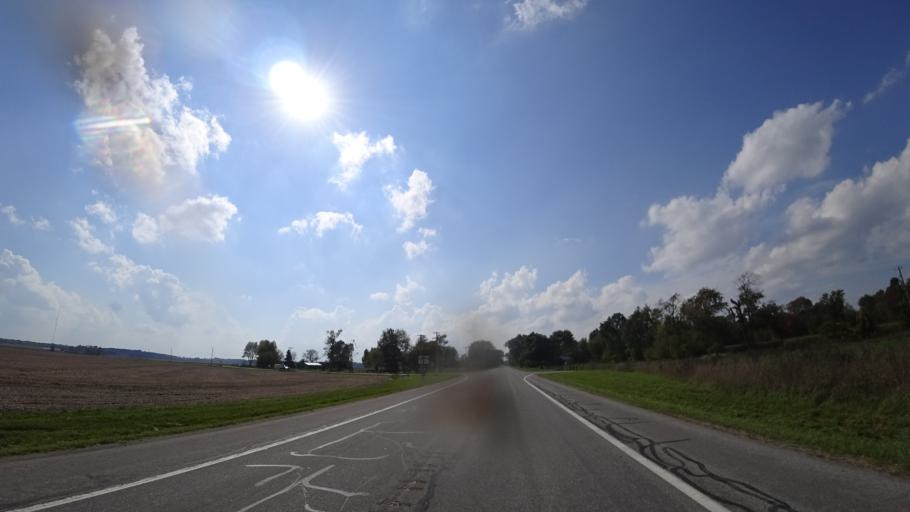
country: US
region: Michigan
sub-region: Saint Joseph County
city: Colon
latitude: 42.0344
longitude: -85.3311
